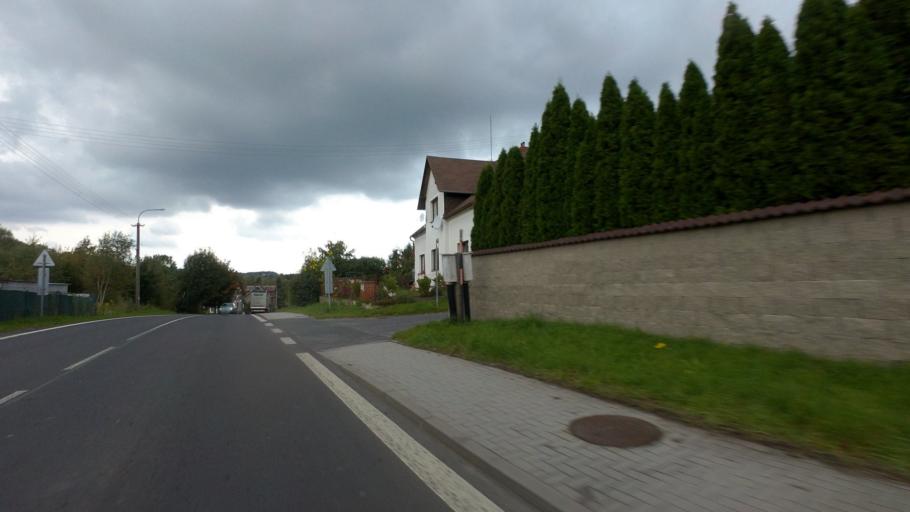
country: CZ
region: Ustecky
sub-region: Okres Decin
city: Rumburk
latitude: 50.9579
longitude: 14.5426
